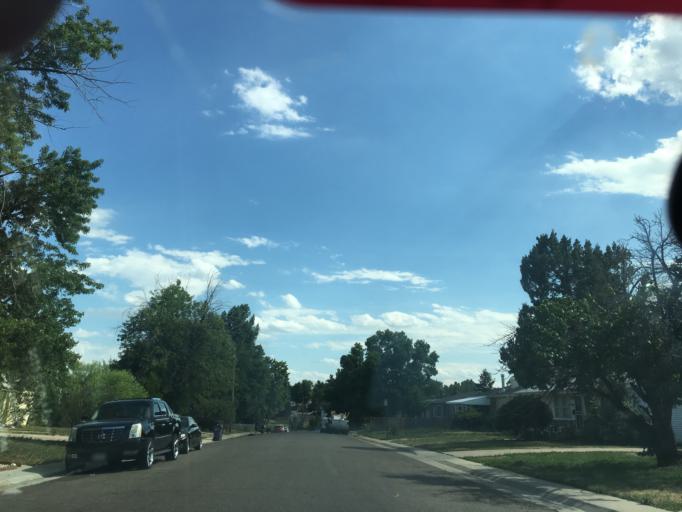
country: US
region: Colorado
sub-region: Arapahoe County
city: Sheridan
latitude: 39.6872
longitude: -105.0391
